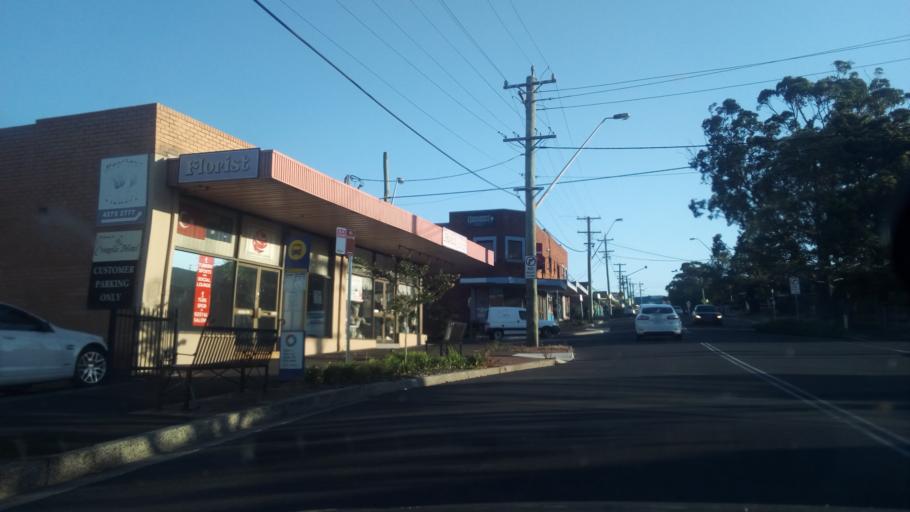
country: AU
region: New South Wales
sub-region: Wollongong
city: Cringila
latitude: -34.4663
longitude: 150.8725
